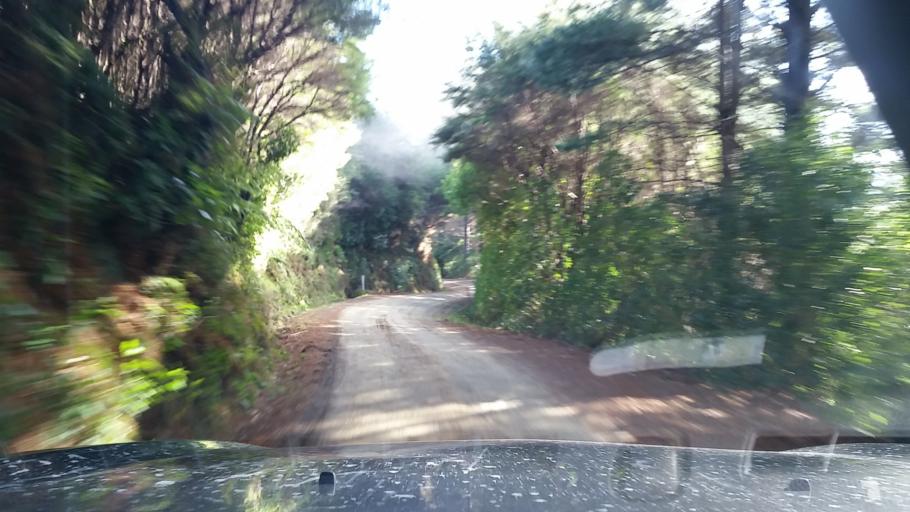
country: NZ
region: Marlborough
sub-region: Marlborough District
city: Picton
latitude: -41.1630
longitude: 173.9737
